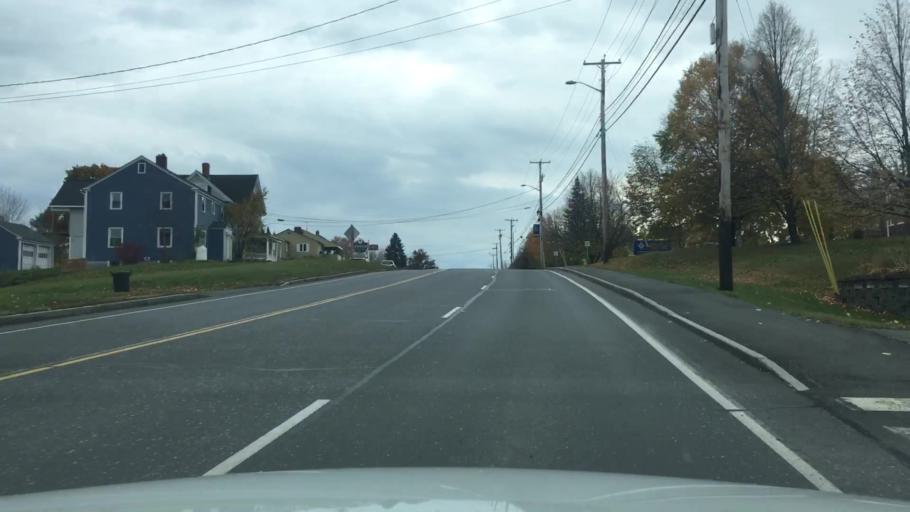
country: US
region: Maine
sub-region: Aroostook County
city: Presque Isle
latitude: 46.6733
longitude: -68.0157
